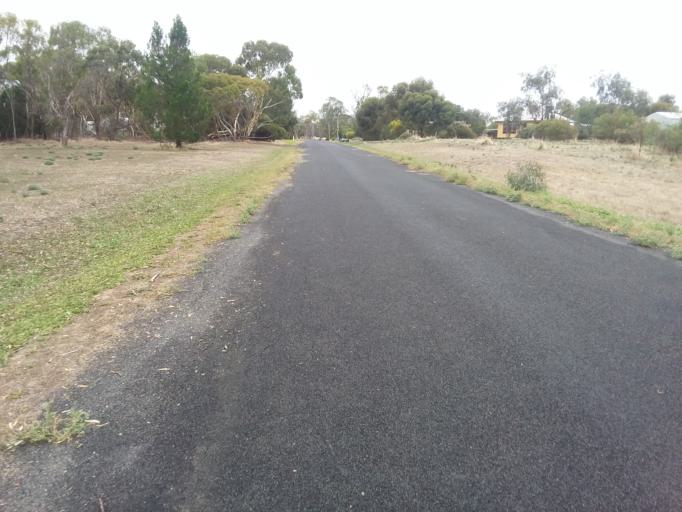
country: AU
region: Victoria
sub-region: Horsham
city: Horsham
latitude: -36.7415
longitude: 141.9365
